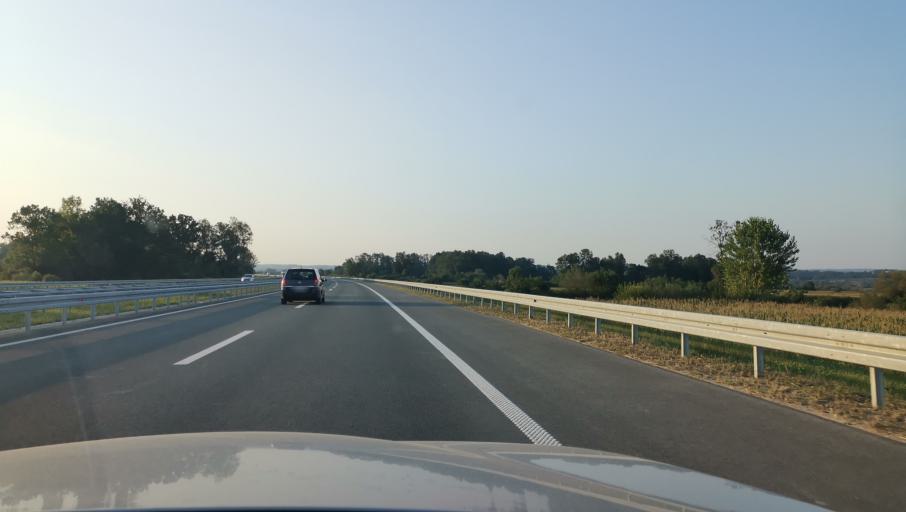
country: RS
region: Central Serbia
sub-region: Kolubarski Okrug
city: Ljig
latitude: 44.2666
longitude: 20.2701
